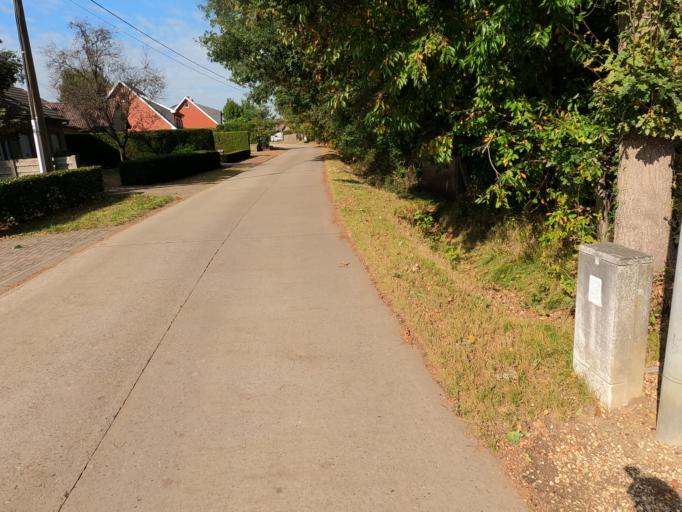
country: BE
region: Flanders
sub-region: Provincie Antwerpen
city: Lille
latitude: 51.2312
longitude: 4.8272
